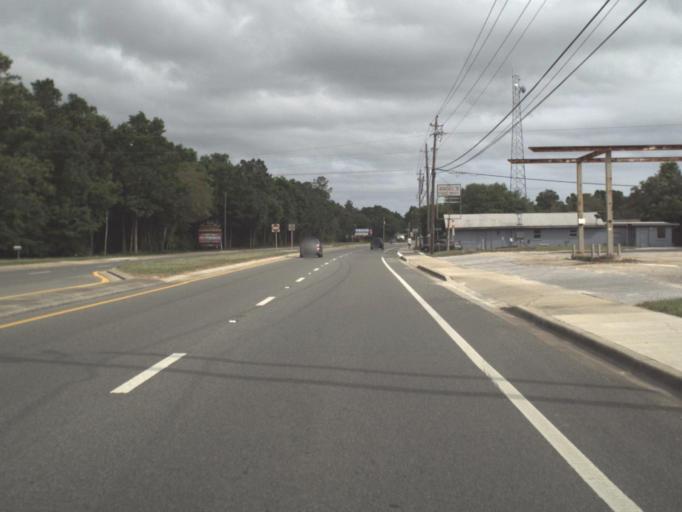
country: US
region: Florida
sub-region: Santa Rosa County
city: Milton
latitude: 30.6592
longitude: -87.0489
